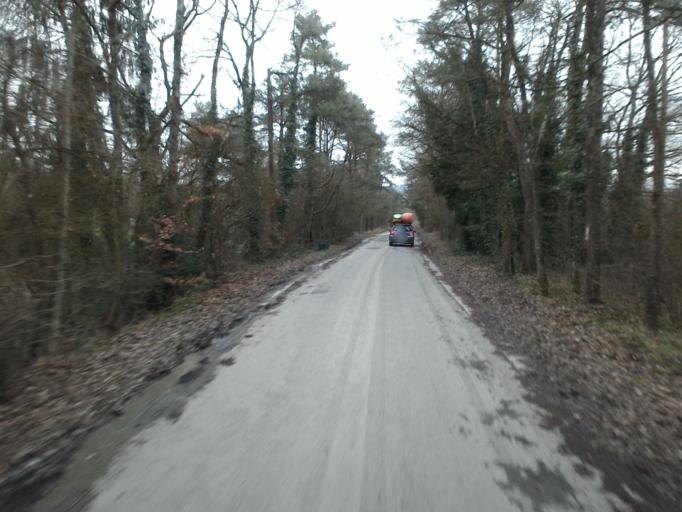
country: BE
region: Wallonia
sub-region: Province du Luxembourg
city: Wellin
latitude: 50.1113
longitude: 5.1344
